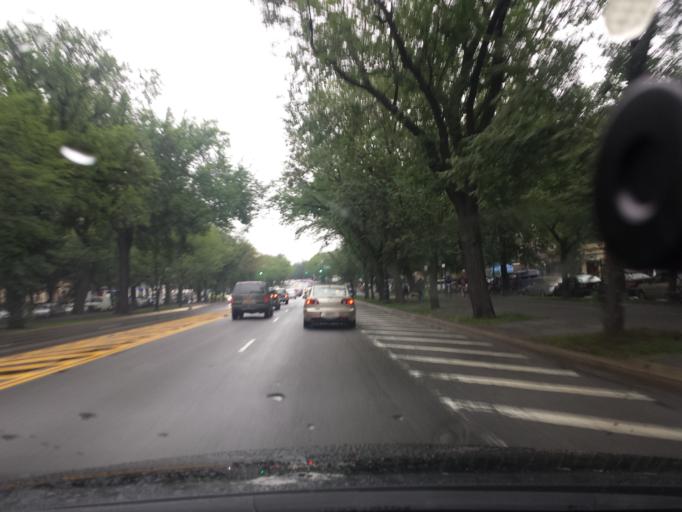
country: US
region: New York
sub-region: Kings County
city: Brooklyn
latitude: 40.6710
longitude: -73.9597
